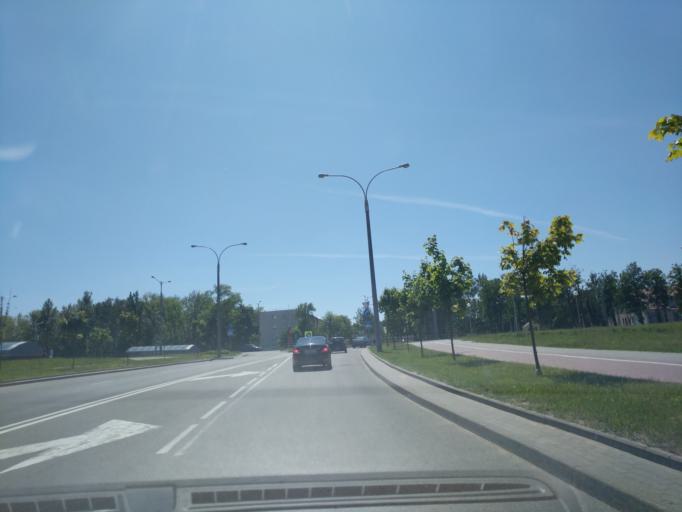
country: BY
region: Minsk
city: Zhdanovichy
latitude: 53.9101
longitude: 27.4178
